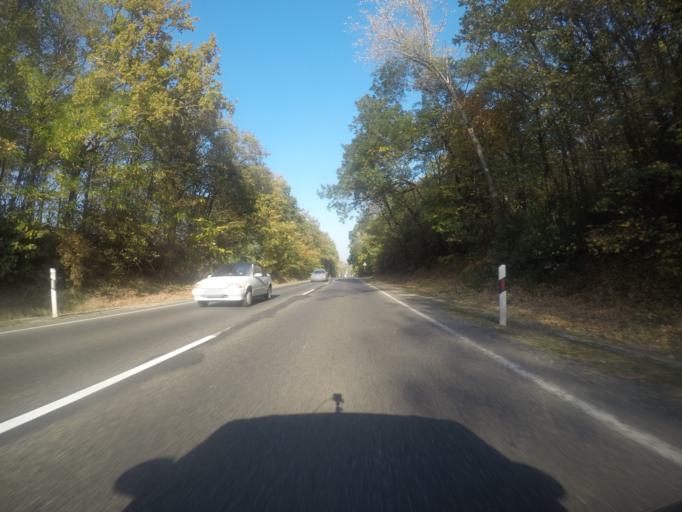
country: HU
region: Fejer
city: dunaujvaros
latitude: 46.9870
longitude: 18.9183
